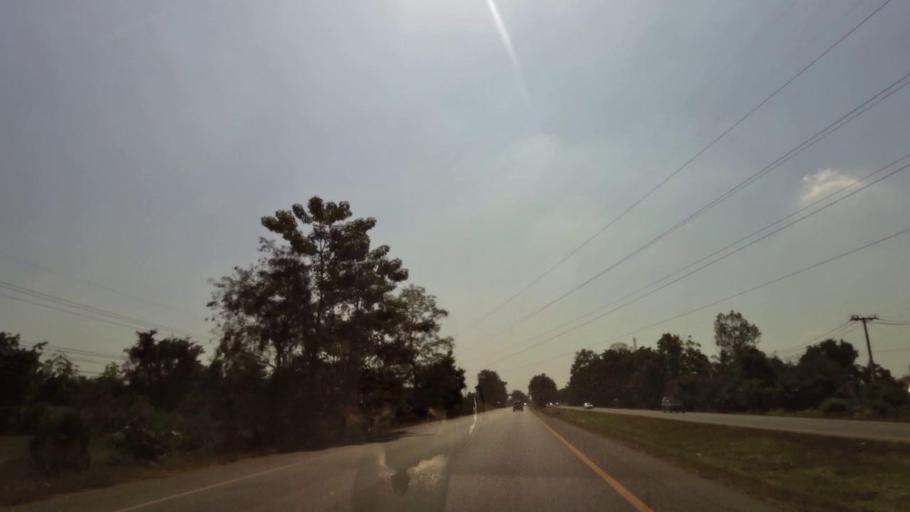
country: TH
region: Phichit
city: Wachira Barami
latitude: 16.3918
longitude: 100.1391
